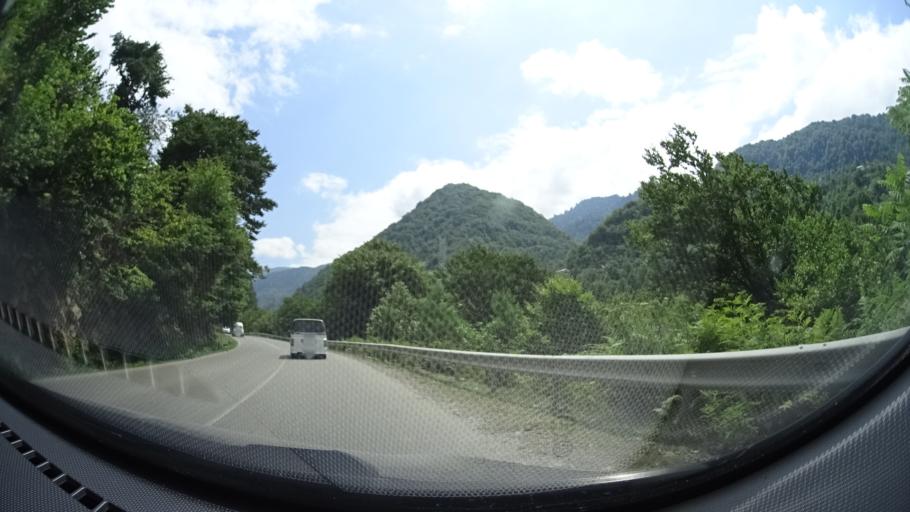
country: TR
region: Artvin
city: Camili
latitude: 41.5665
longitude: 41.8372
